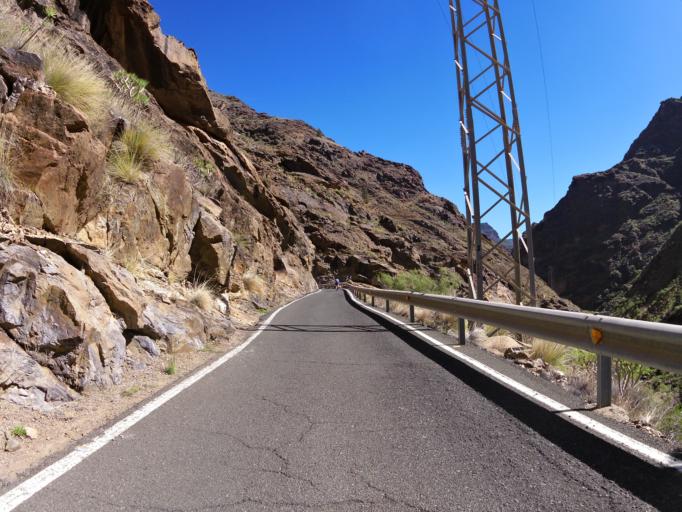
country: ES
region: Canary Islands
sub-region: Provincia de Las Palmas
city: San Nicolas
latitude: 27.9876
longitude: -15.7206
